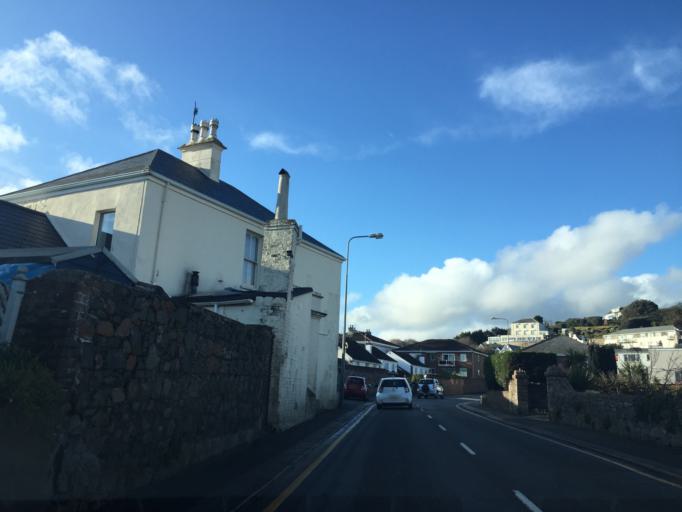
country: JE
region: St Helier
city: Saint Helier
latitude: 49.1974
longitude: -2.1382
